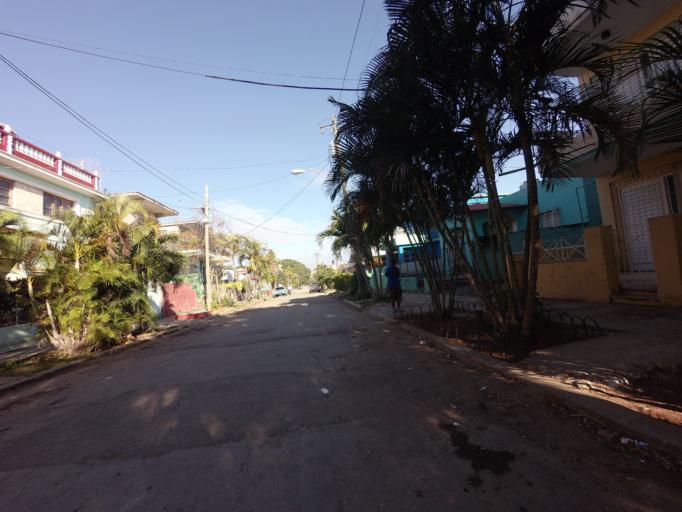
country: CU
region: La Habana
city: Cerro
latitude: 23.1022
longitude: -82.4318
